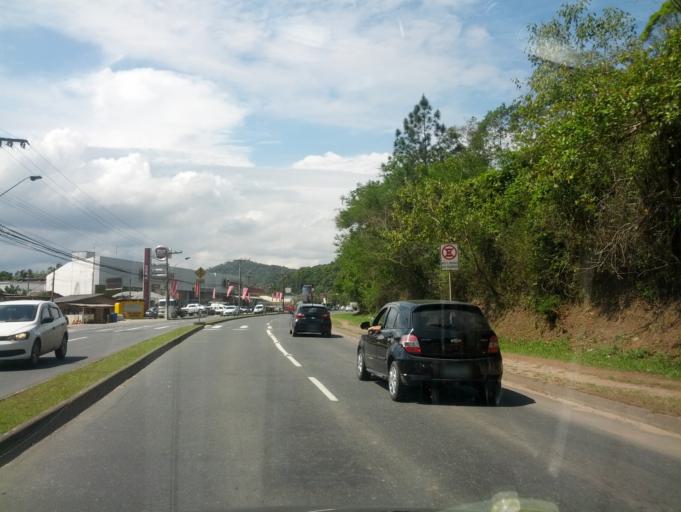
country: BR
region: Santa Catarina
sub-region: Blumenau
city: Blumenau
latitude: -26.9053
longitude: -49.0655
